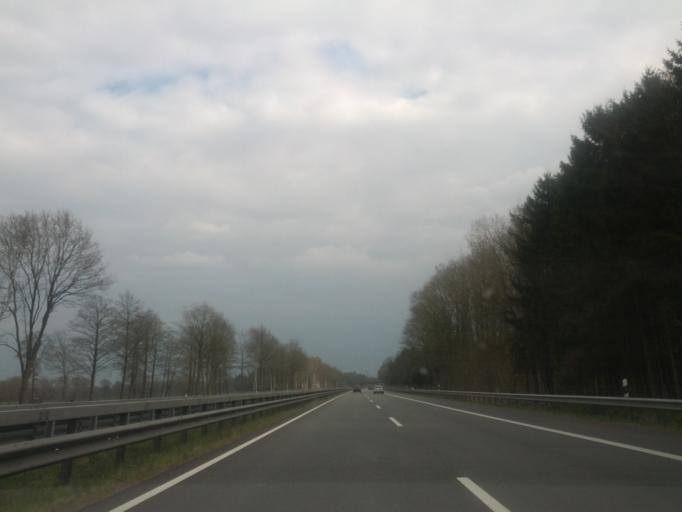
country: DE
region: Lower Saxony
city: Westerstede
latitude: 53.2520
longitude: 7.9772
